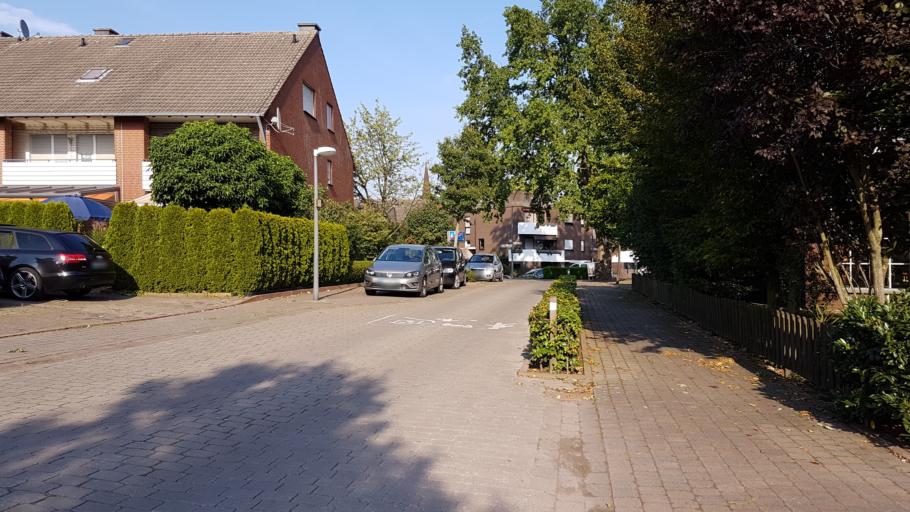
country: DE
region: North Rhine-Westphalia
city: Olfen
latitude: 51.7053
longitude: 7.3739
